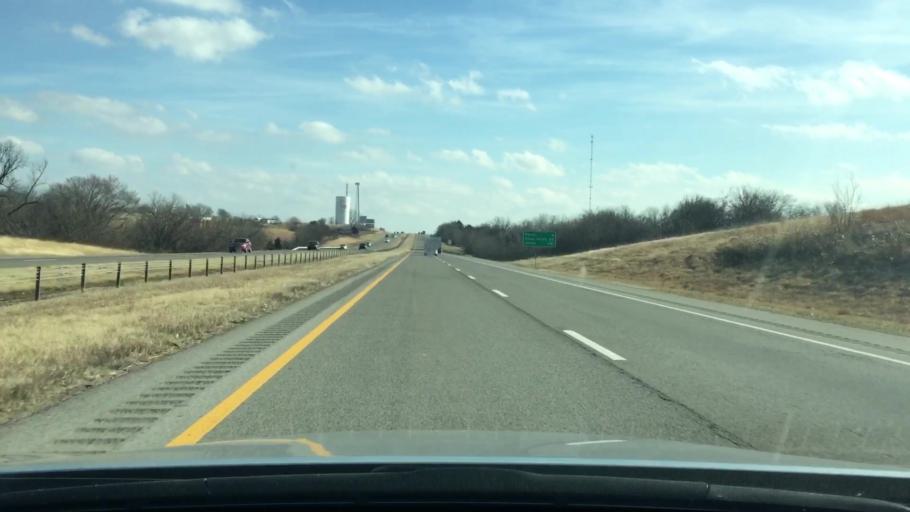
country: US
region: Oklahoma
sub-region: Cleveland County
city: Slaughterville
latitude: 35.0713
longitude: -97.4004
